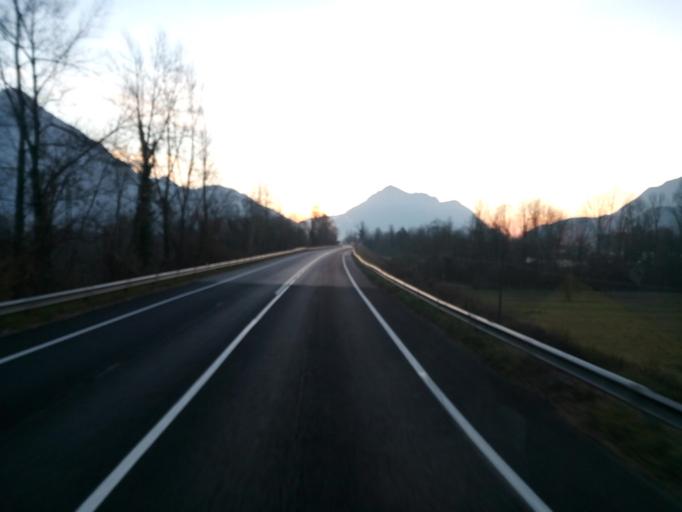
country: IT
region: Friuli Venezia Giulia
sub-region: Provincia di Udine
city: Chiaulis
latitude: 46.4044
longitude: 12.9937
